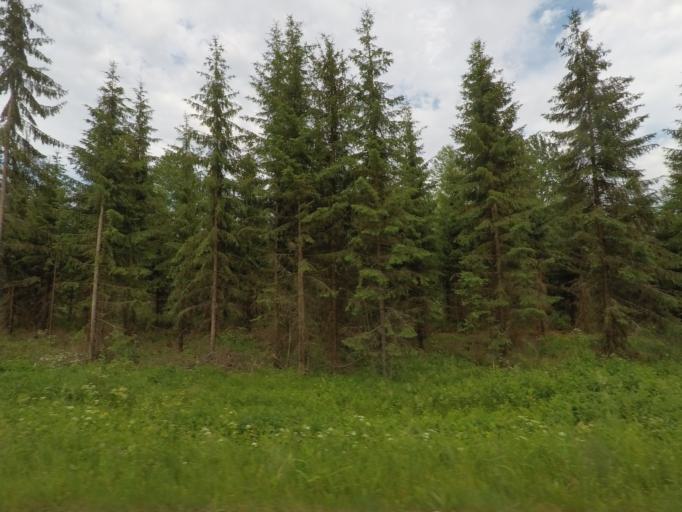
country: FI
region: Paijanne Tavastia
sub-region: Lahti
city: Hollola
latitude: 60.8681
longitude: 25.5015
